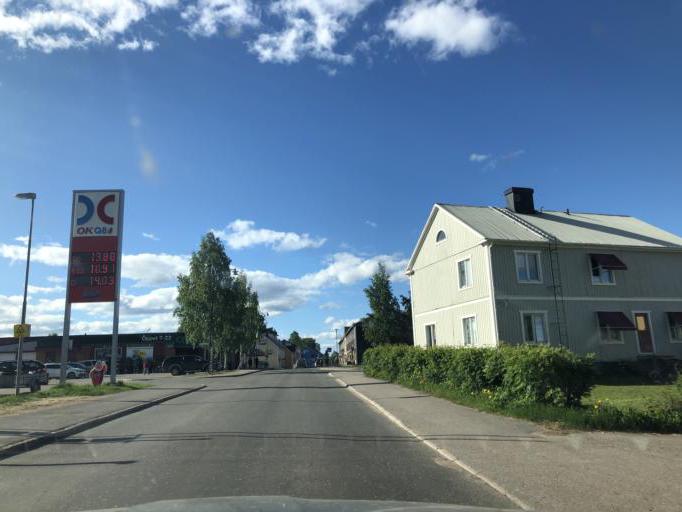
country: SE
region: Norrbotten
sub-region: Overkalix Kommun
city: OEverkalix
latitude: 66.3245
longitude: 22.8468
